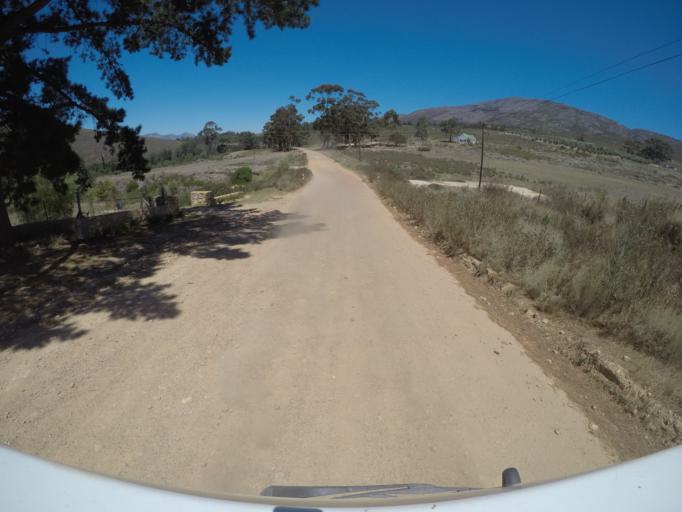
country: ZA
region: Western Cape
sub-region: Overberg District Municipality
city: Caledon
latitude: -34.1794
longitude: 19.2243
